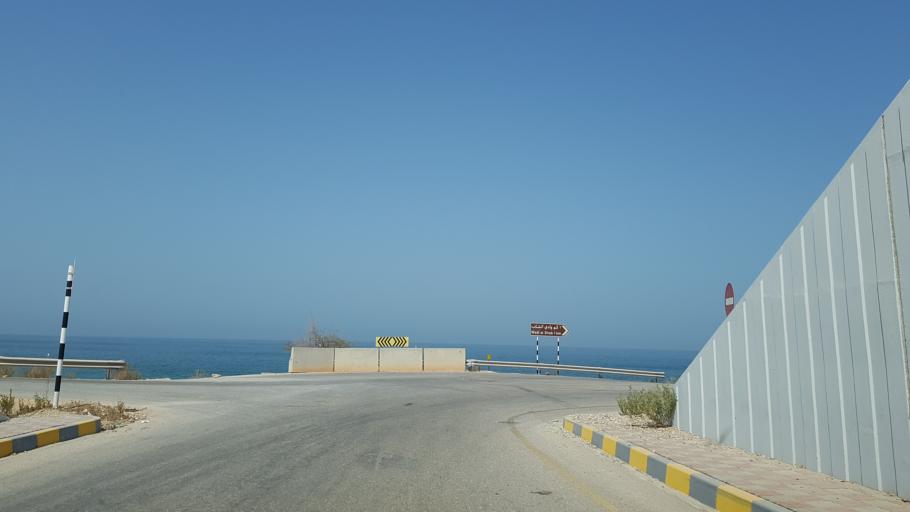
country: OM
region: Ash Sharqiyah
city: Sur
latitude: 22.8448
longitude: 59.2408
